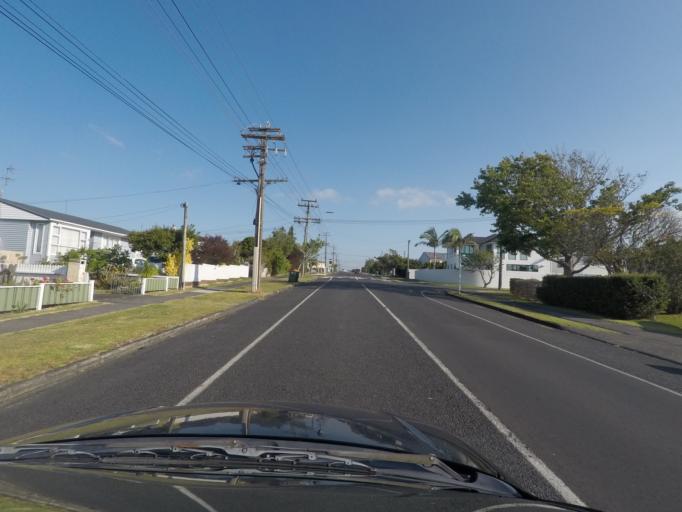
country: NZ
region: Auckland
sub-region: Auckland
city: Rosebank
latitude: -36.8577
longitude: 174.6430
